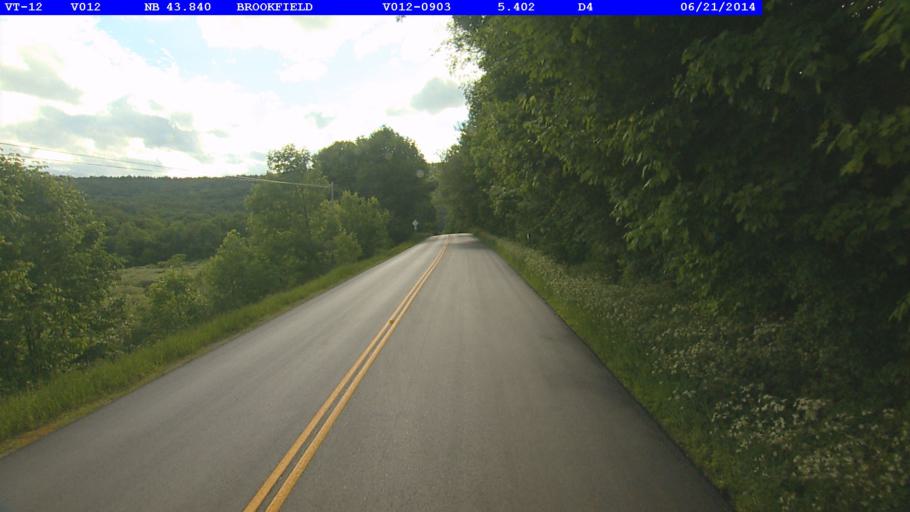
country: US
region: Vermont
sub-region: Washington County
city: Northfield
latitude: 44.0759
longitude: -72.6405
